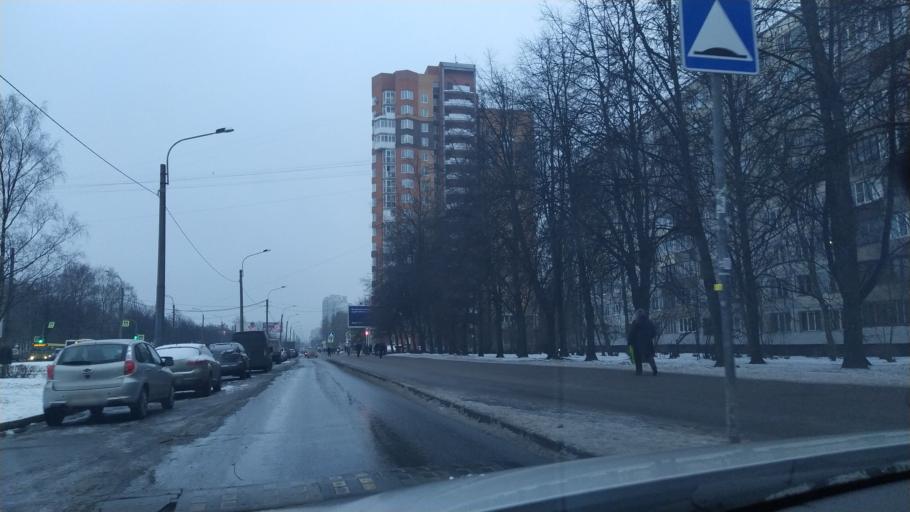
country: RU
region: Leningrad
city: Akademicheskoe
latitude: 60.0182
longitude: 30.4021
